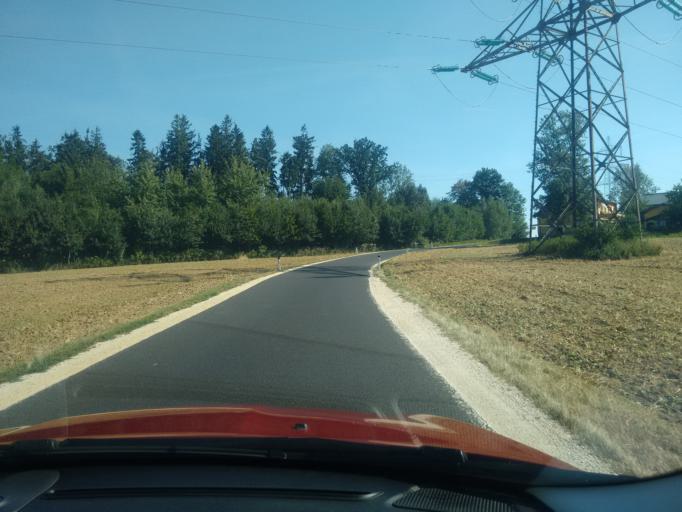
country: AT
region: Upper Austria
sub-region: Wels-Land
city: Sattledt
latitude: 48.0841
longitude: 14.0723
